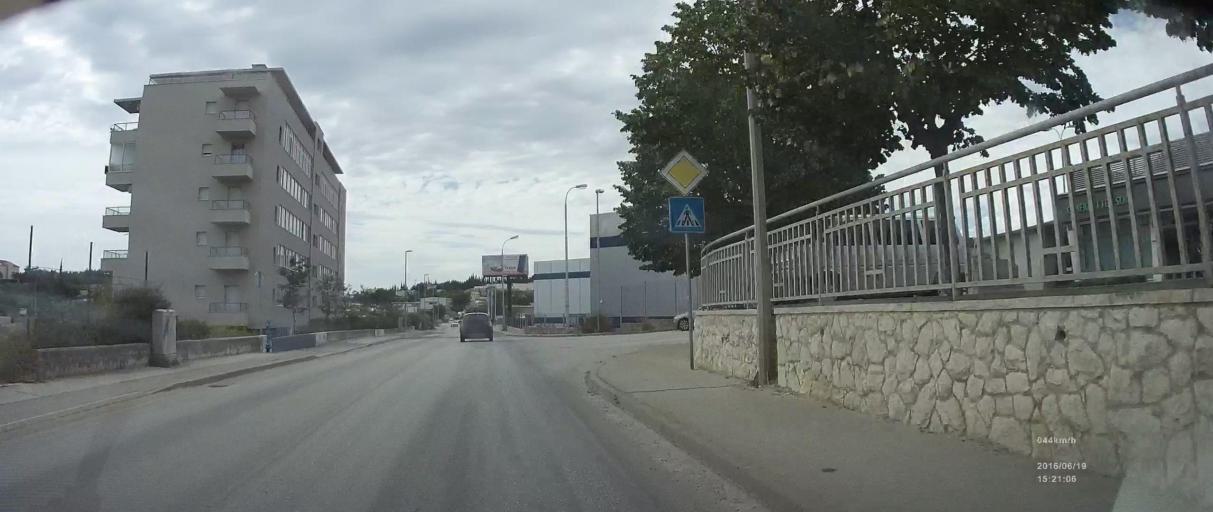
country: HR
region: Splitsko-Dalmatinska
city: Kamen
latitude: 43.5078
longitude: 16.5044
